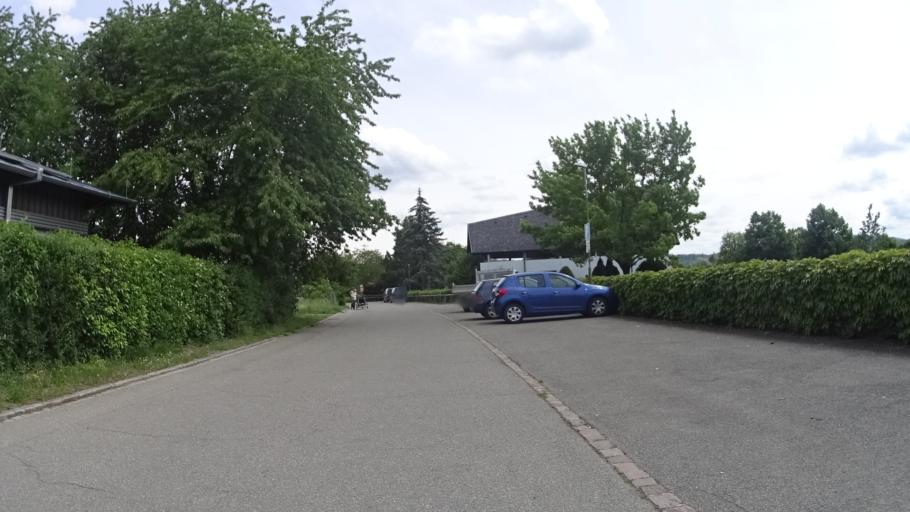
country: CH
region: Aargau
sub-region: Bezirk Rheinfelden
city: Kaiseraugst
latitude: 47.5565
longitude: 7.7371
